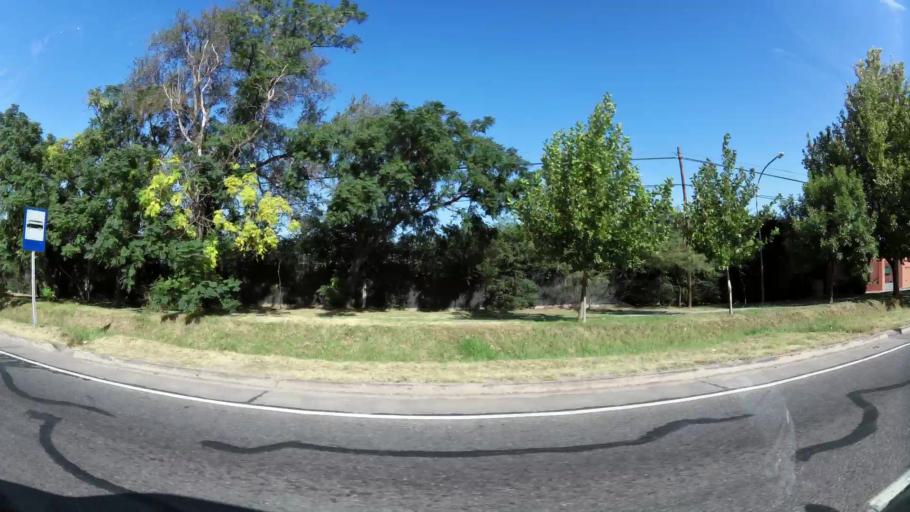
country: AR
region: Cordoba
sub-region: Departamento de Capital
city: Cordoba
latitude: -31.4826
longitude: -64.2427
